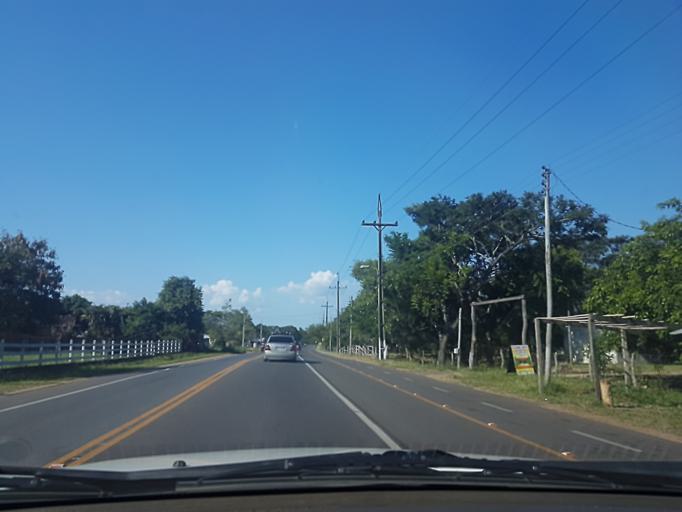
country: PY
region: Central
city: Aregua
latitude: -25.2332
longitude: -57.4200
